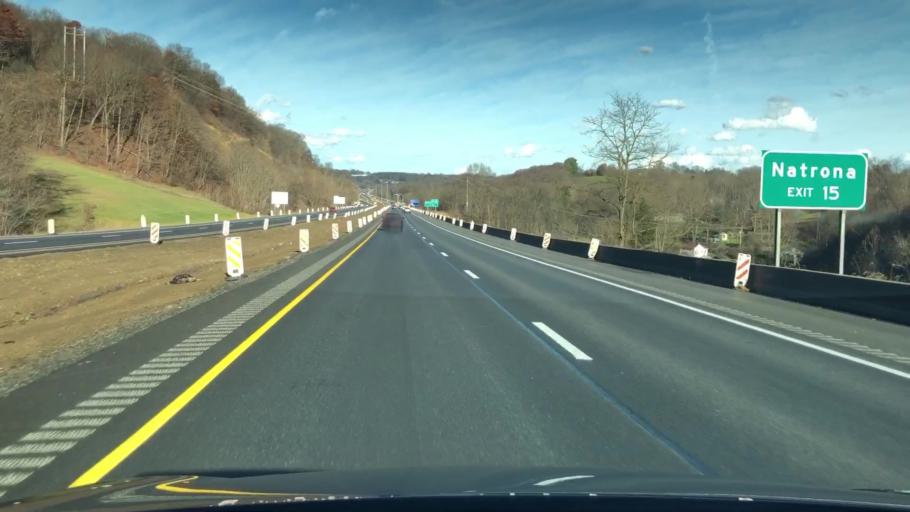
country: US
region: Pennsylvania
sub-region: Allegheny County
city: Brackenridge
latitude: 40.6225
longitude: -79.7440
